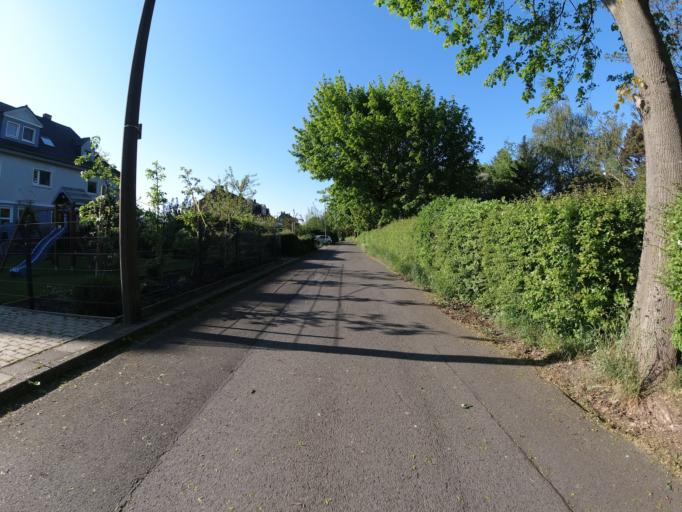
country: DE
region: North Rhine-Westphalia
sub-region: Regierungsbezirk Dusseldorf
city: Hochfeld
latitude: 51.3859
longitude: 6.7086
